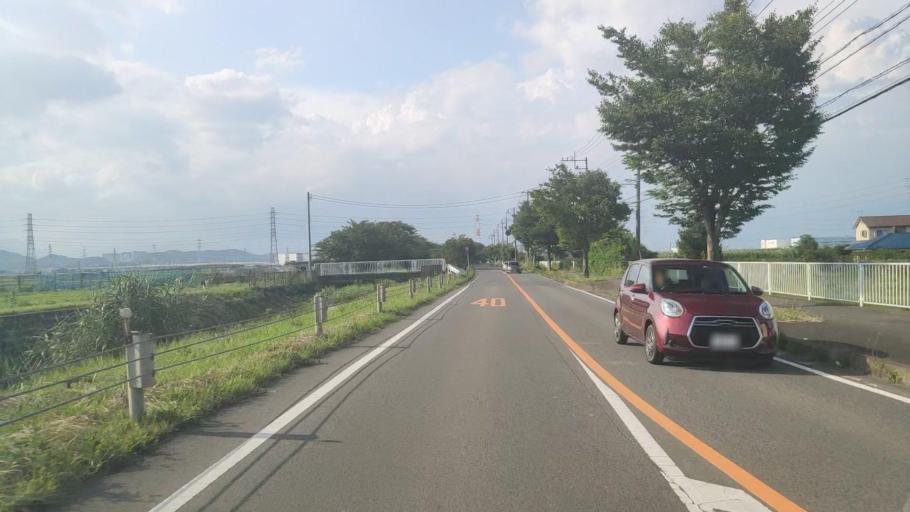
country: JP
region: Kanagawa
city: Isehara
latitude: 35.3918
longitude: 139.3379
